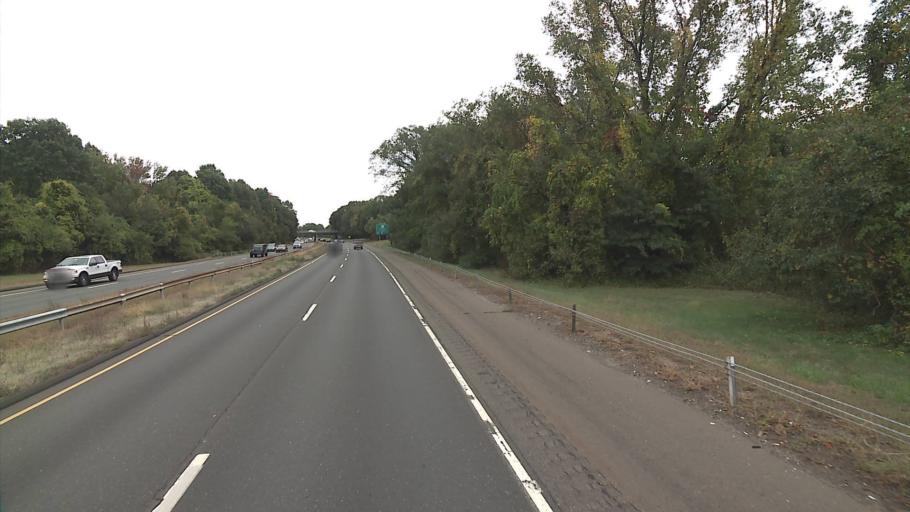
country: US
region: Connecticut
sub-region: New Haven County
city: New Haven
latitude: 41.3550
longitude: -72.9504
